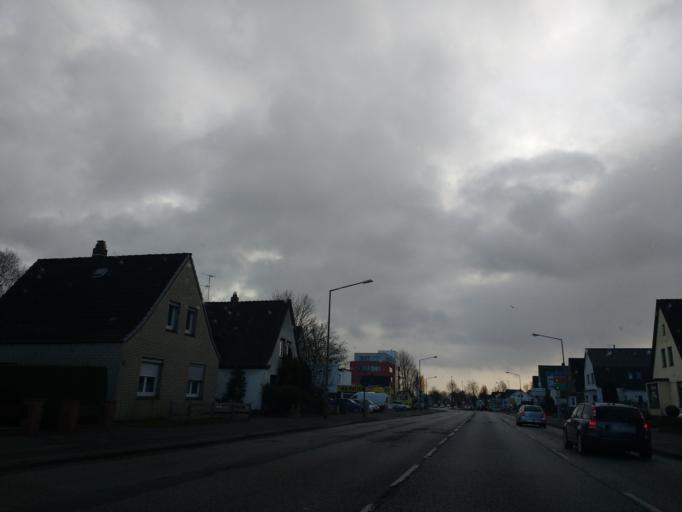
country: DE
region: Schleswig-Holstein
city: Neumunster
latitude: 54.0908
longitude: 9.9749
